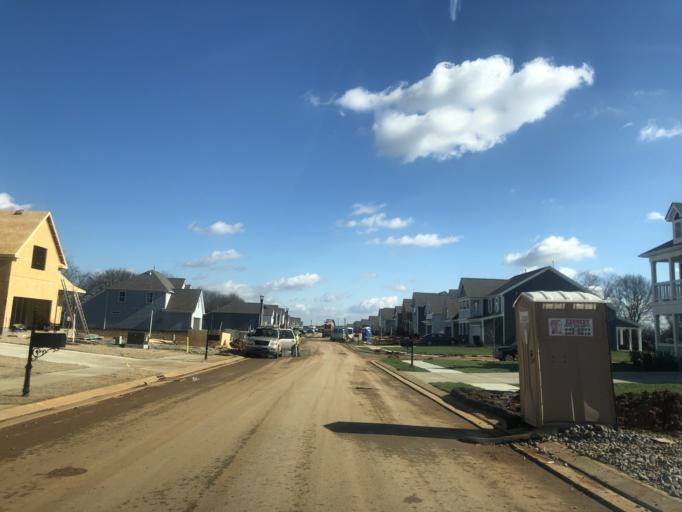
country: US
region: Tennessee
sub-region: Rutherford County
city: Smyrna
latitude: 35.8867
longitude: -86.4871
